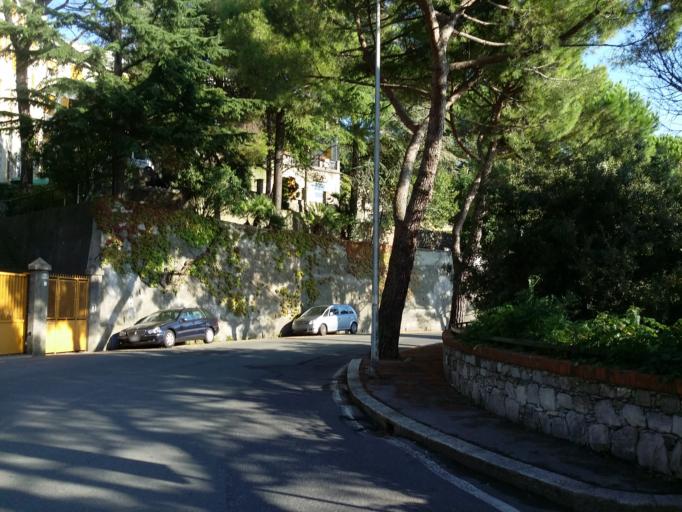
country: IT
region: Liguria
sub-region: Provincia di Genova
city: Genoa
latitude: 44.4202
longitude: 8.9390
